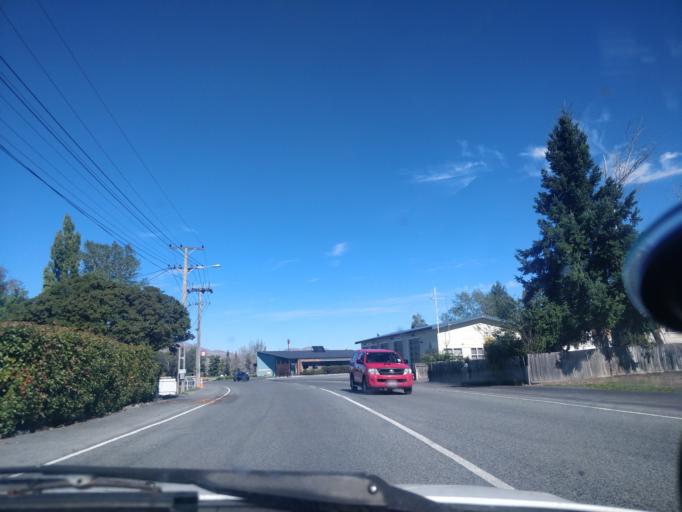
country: NZ
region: Canterbury
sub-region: Timaru District
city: Pleasant Point
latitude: -44.2597
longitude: 170.0982
